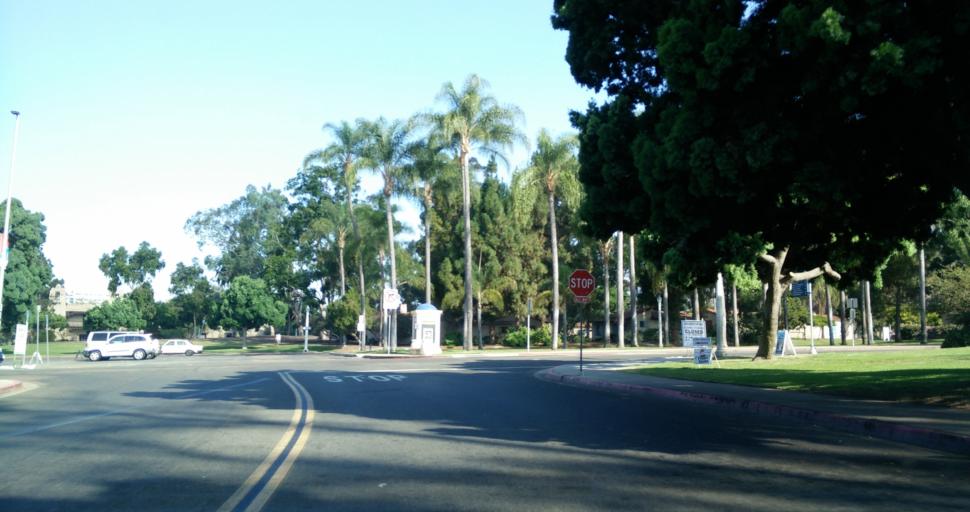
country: US
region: California
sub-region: San Diego County
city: San Diego
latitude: 32.7280
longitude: -117.1519
